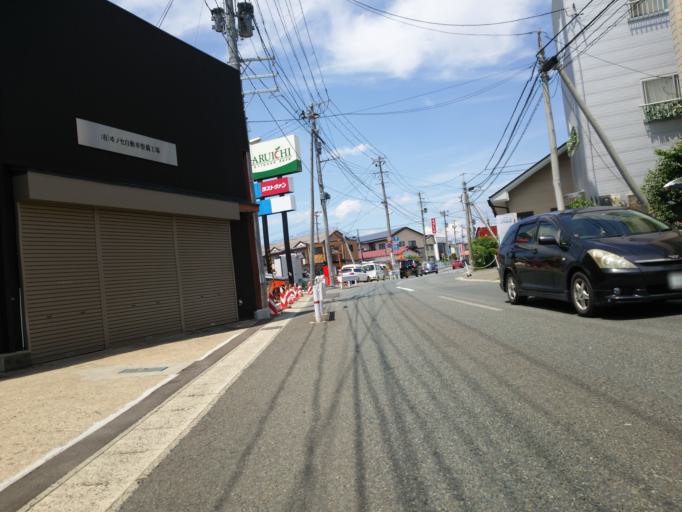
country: JP
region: Iwate
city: Morioka-shi
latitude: 39.7121
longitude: 141.1189
